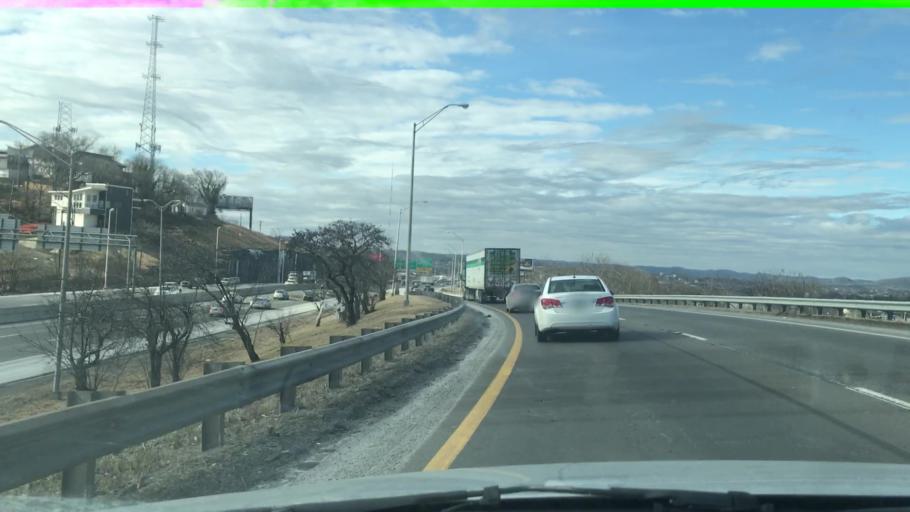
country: US
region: Tennessee
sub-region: Davidson County
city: Nashville
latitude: 36.1567
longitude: -86.8262
